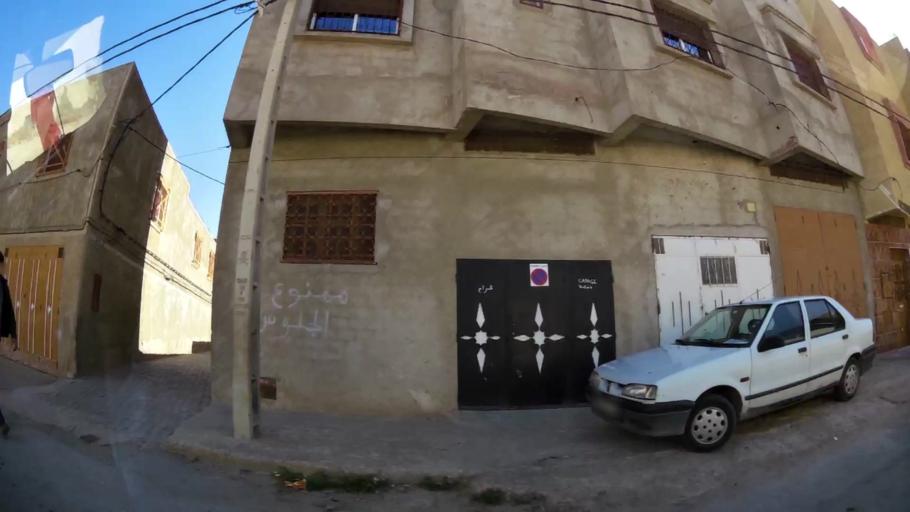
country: MA
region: Oriental
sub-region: Oujda-Angad
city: Oujda
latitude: 34.6893
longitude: -1.9292
